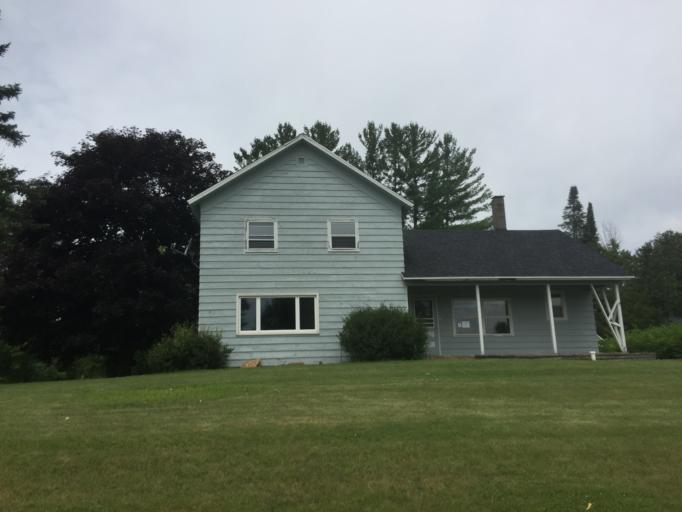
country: US
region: Wisconsin
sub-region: Oconto County
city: Oconto Falls
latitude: 44.9057
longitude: -88.0127
